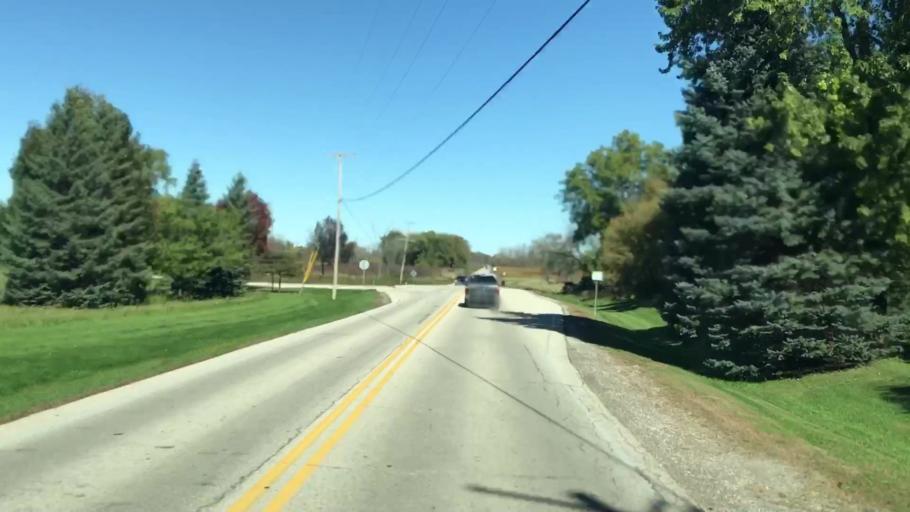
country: US
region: Wisconsin
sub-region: Waukesha County
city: Brookfield
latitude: 43.0729
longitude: -88.1662
